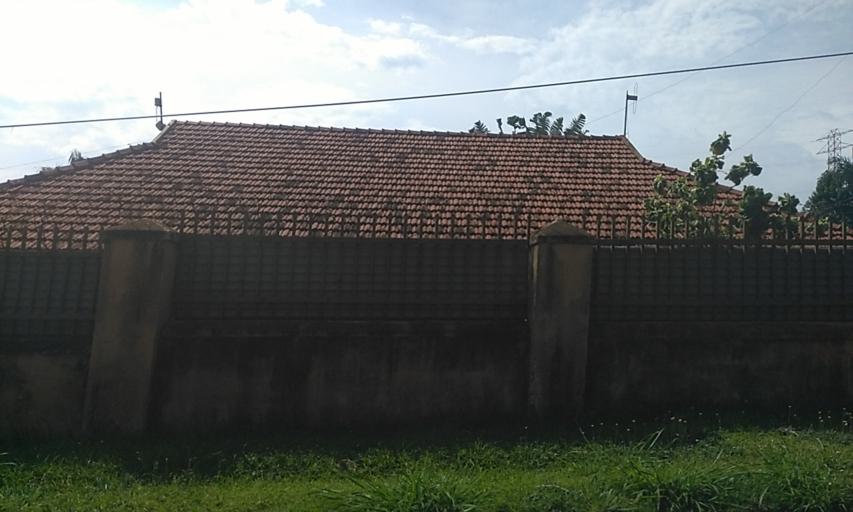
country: UG
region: Central Region
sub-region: Wakiso District
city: Kireka
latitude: 0.3567
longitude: 32.6189
